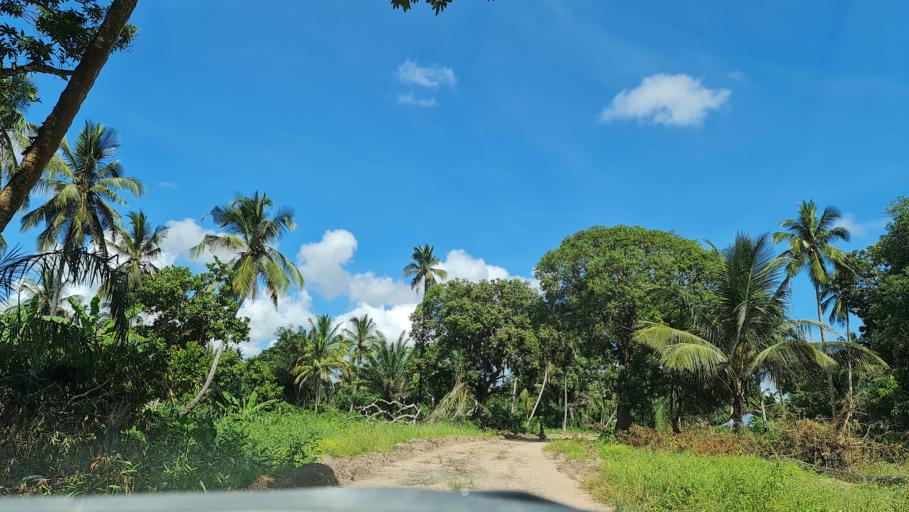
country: MZ
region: Zambezia
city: Quelimane
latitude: -17.3846
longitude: 37.5247
